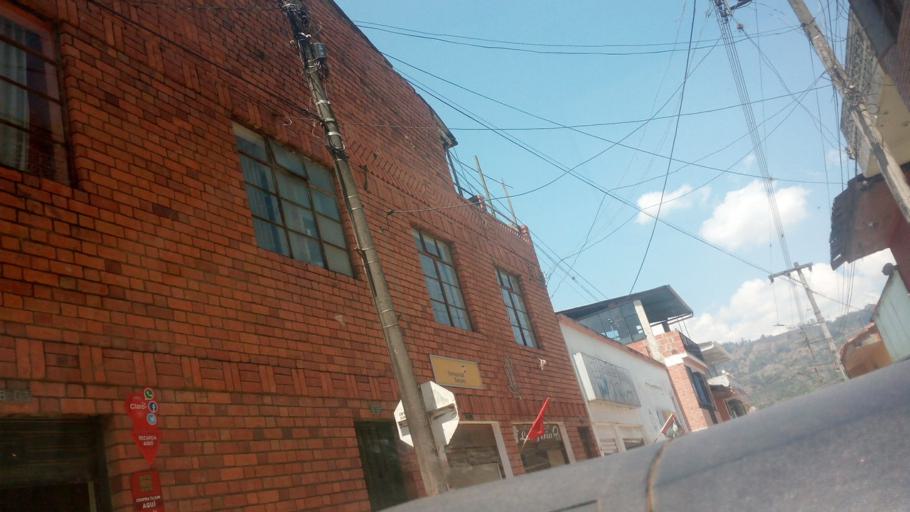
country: CO
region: Boyaca
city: Guateque
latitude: 5.0079
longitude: -73.4724
